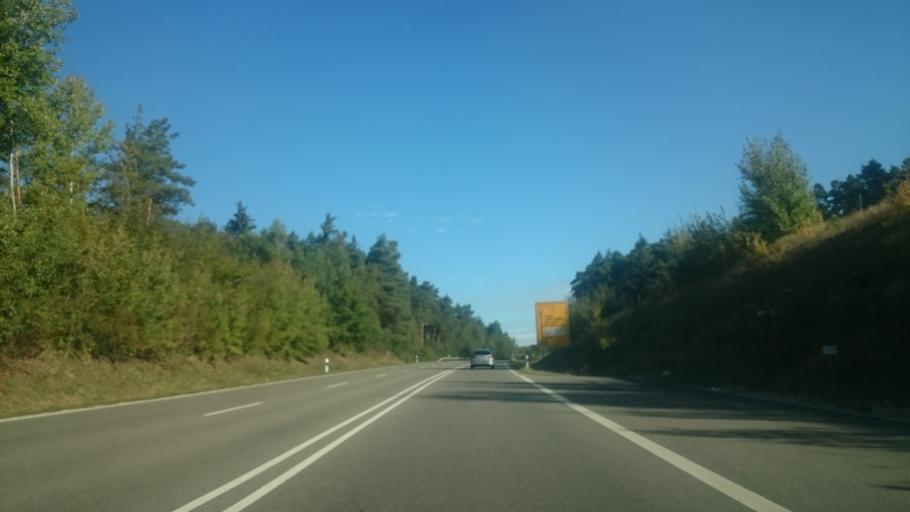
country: DE
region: Bavaria
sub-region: Regierungsbezirk Mittelfranken
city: Pleinfeld
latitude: 49.1064
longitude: 10.9966
